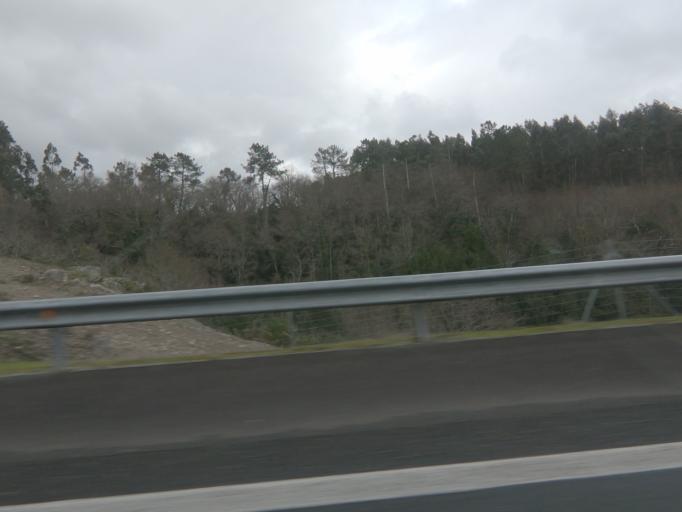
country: ES
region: Galicia
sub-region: Provincia da Coruna
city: Vedra
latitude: 42.7940
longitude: -8.4817
